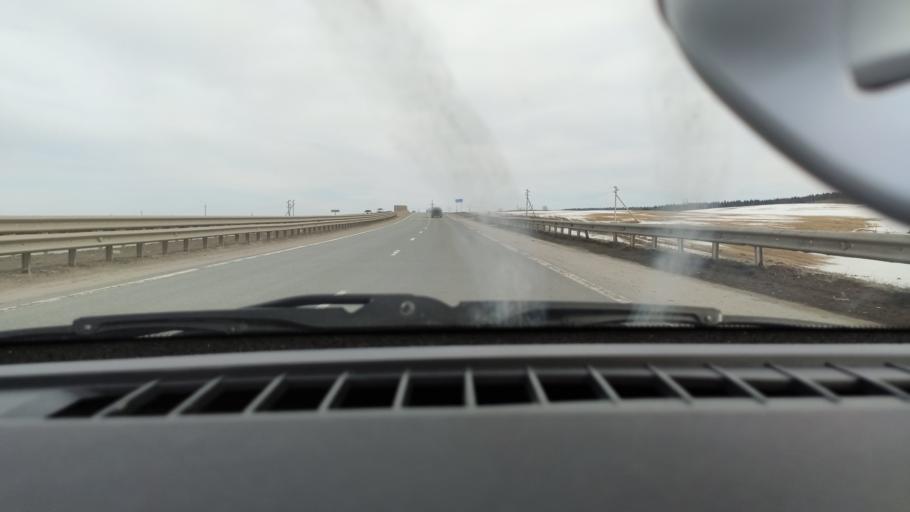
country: RU
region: Perm
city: Ferma
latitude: 57.9322
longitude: 56.3467
